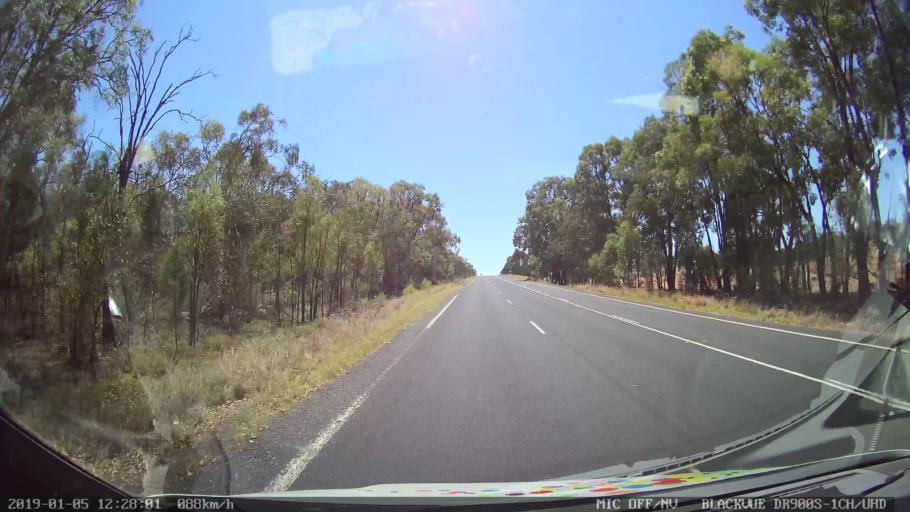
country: AU
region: New South Wales
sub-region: Warrumbungle Shire
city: Coonabarabran
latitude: -31.2435
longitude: 149.3171
